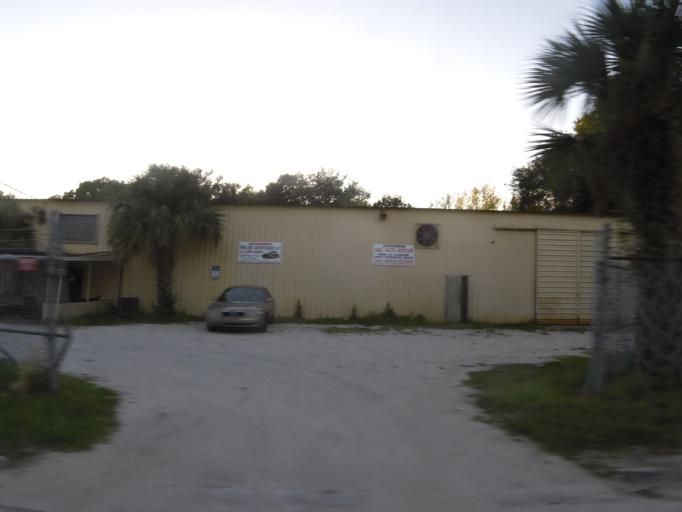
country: US
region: Florida
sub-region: Duval County
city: Jacksonville
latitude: 30.3534
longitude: -81.6412
